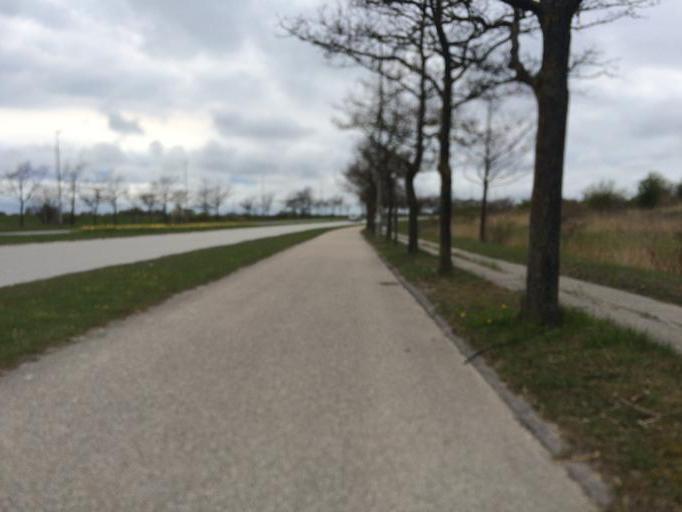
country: DK
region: Capital Region
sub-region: Hvidovre Kommune
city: Hvidovre
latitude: 55.6138
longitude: 12.4486
